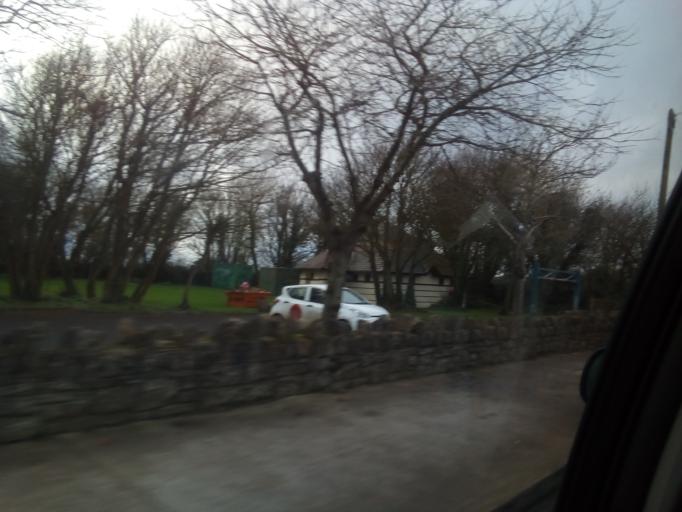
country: IE
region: Leinster
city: An Ros
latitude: 53.5401
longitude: -6.0937
